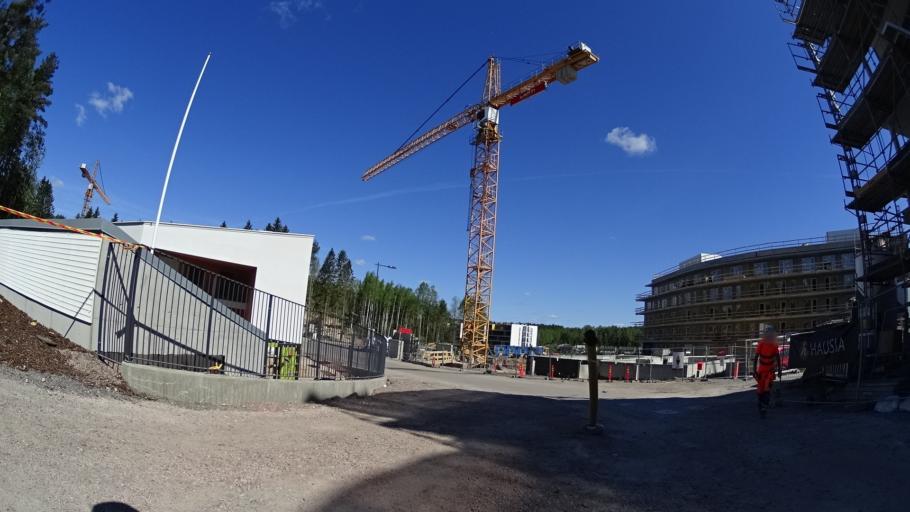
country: FI
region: Uusimaa
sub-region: Helsinki
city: Espoo
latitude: 60.1638
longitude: 24.6229
